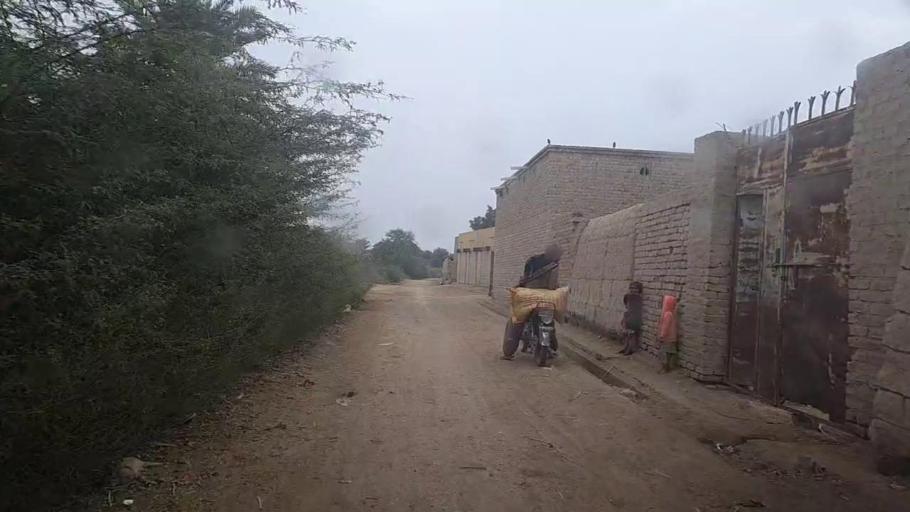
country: PK
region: Sindh
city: Gambat
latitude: 27.3604
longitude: 68.5972
